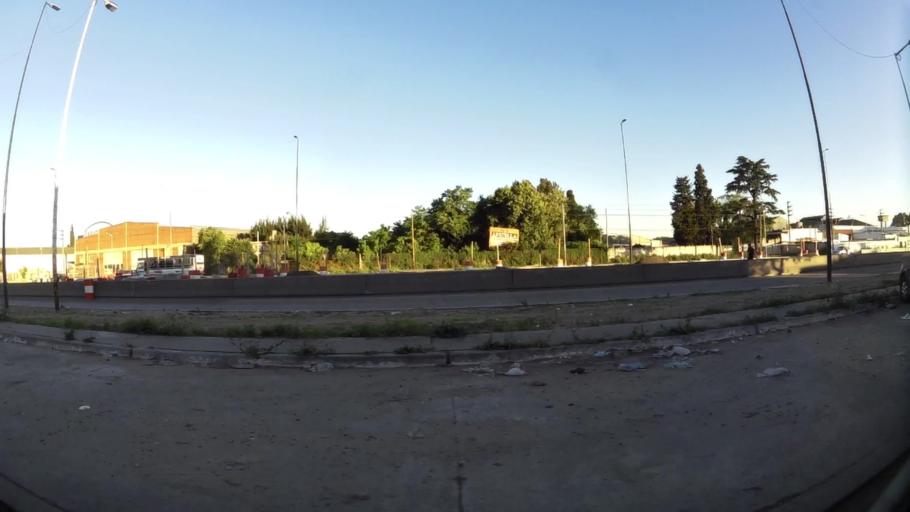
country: AR
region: Buenos Aires
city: San Justo
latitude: -34.7416
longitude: -58.6071
